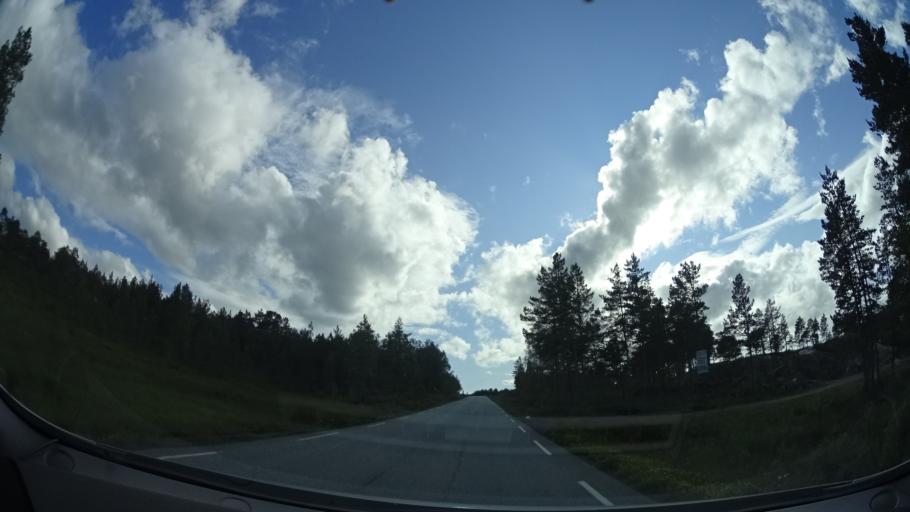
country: NO
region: More og Romsdal
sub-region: Halsa
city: Liaboen
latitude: 63.1298
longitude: 8.3811
